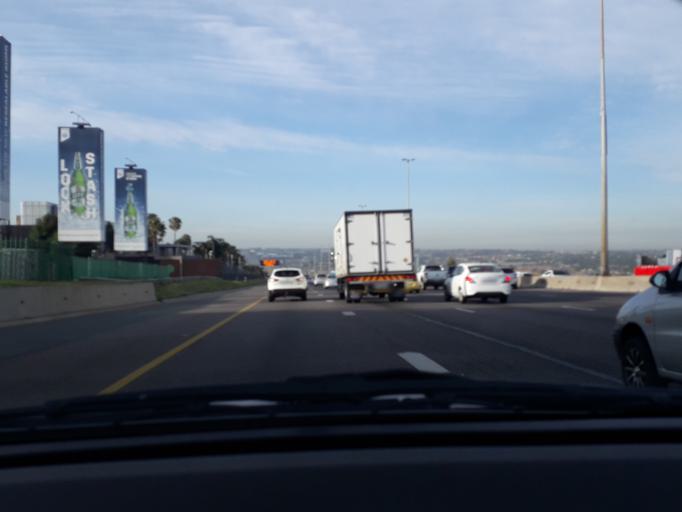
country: ZA
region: Gauteng
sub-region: City of Johannesburg Metropolitan Municipality
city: Midrand
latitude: -25.9409
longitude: 28.1394
